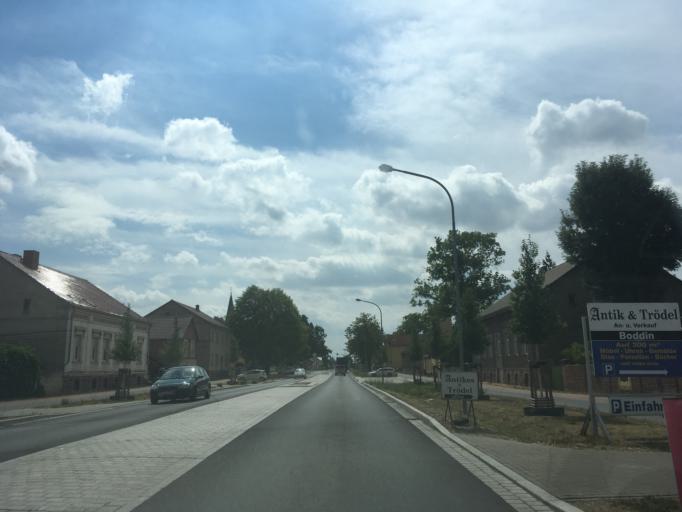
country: DE
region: Brandenburg
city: Dabergotz
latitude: 52.9045
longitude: 12.7282
